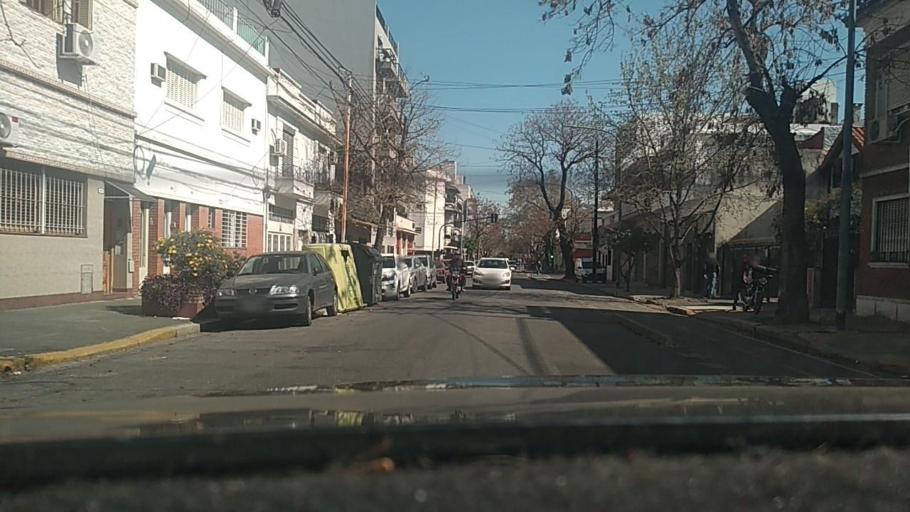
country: AR
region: Buenos Aires F.D.
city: Villa Santa Rita
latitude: -34.6128
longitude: -58.5039
